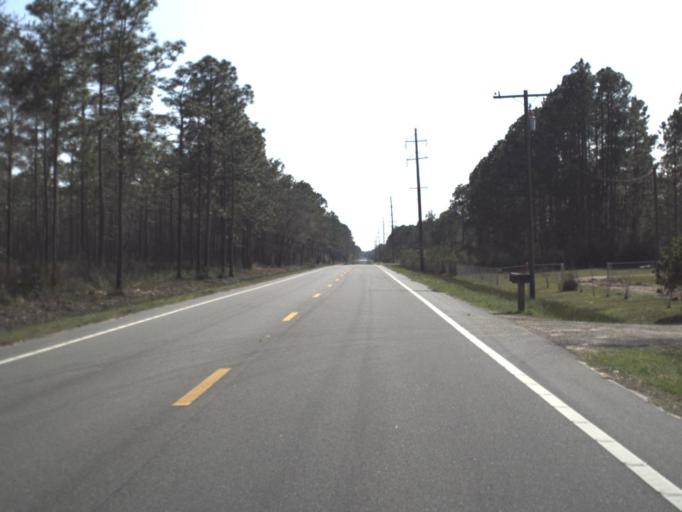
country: US
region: Florida
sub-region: Wakulla County
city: Crawfordville
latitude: 30.0346
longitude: -84.4970
